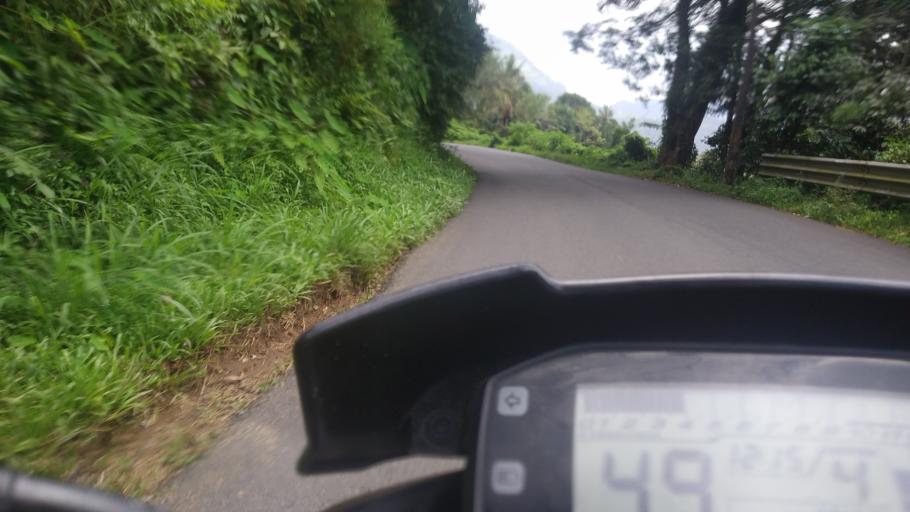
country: IN
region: Kerala
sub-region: Idukki
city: Munnar
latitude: 10.0122
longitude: 77.0095
